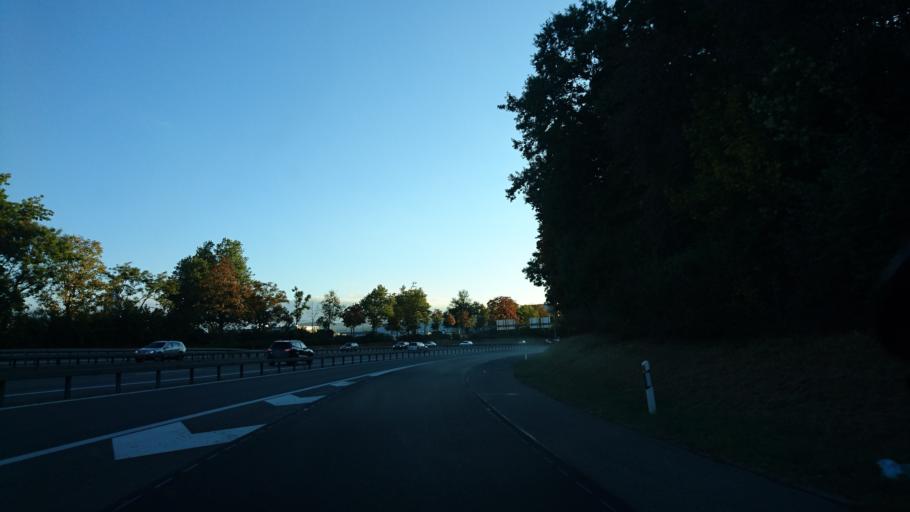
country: CH
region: Bern
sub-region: Bern-Mittelland District
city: Bolligen
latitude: 46.9620
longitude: 7.4747
